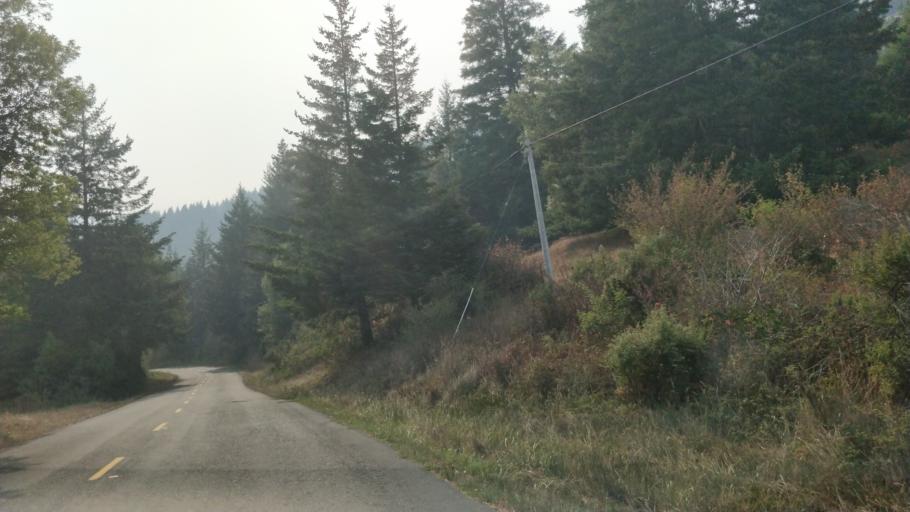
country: US
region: California
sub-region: Humboldt County
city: Rio Dell
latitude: 40.2940
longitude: -124.2497
